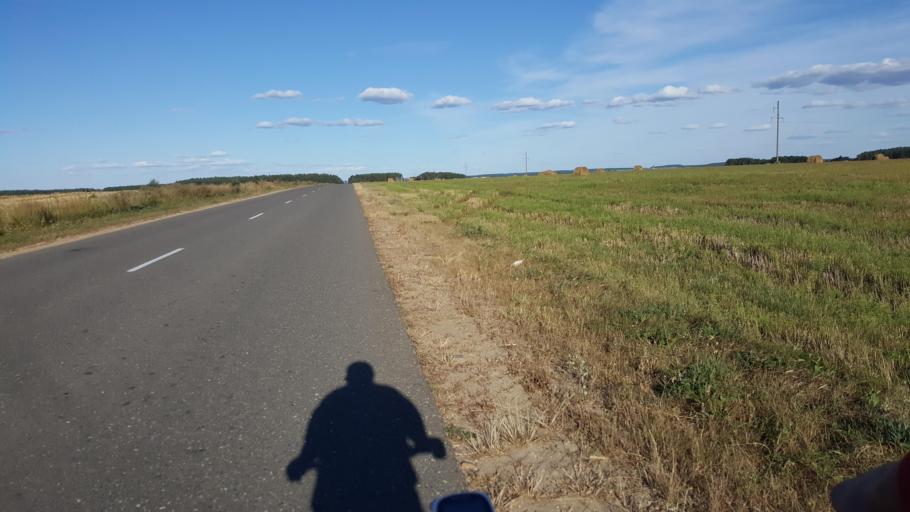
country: BY
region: Brest
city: Kamyanyets
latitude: 52.3860
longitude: 23.7189
